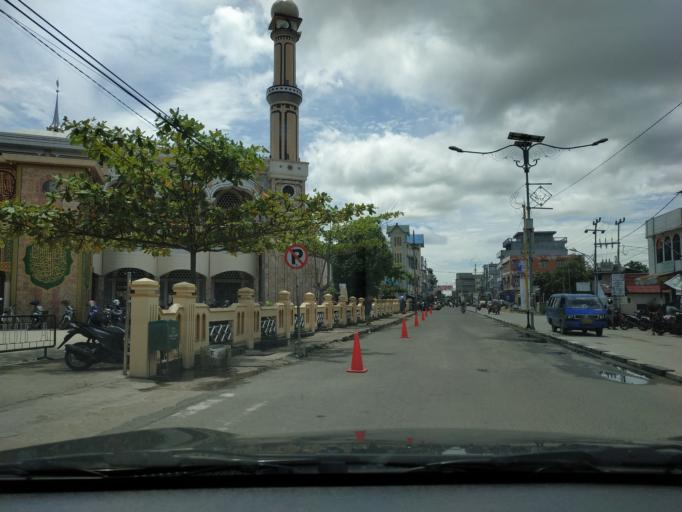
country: ID
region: Riau
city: Tembilahan
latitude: -0.3288
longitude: 103.1566
